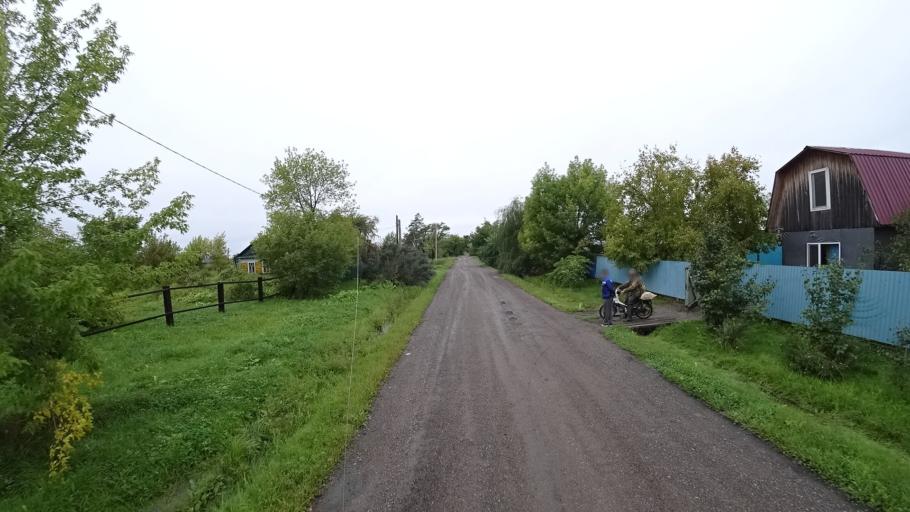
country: RU
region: Primorskiy
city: Monastyrishche
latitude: 44.2119
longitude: 132.4308
